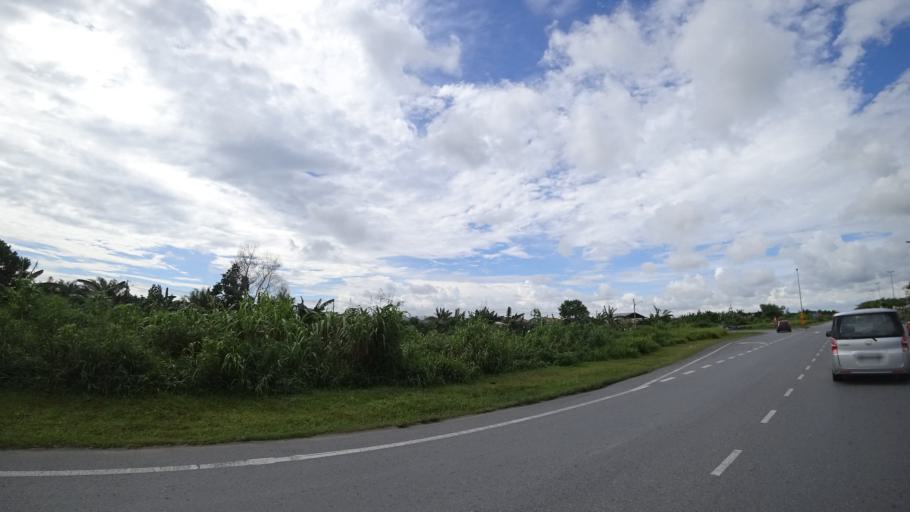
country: MY
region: Sarawak
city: Miri
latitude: 4.4718
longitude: 114.0419
